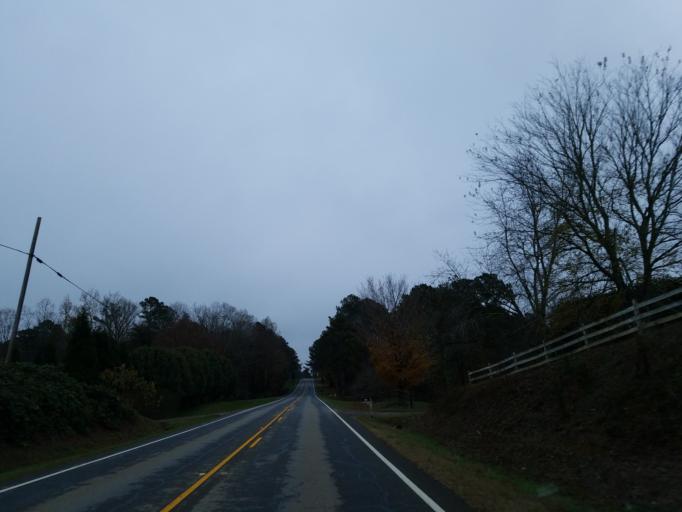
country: US
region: Georgia
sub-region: Pickens County
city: Jasper
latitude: 34.3909
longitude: -84.4529
